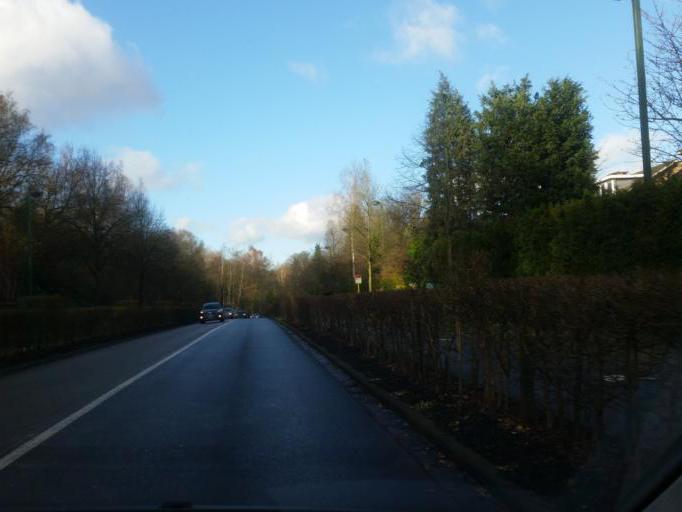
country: BE
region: Flanders
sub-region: Provincie Vlaams-Brabant
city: Hoeilaart
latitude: 50.7870
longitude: 4.4234
